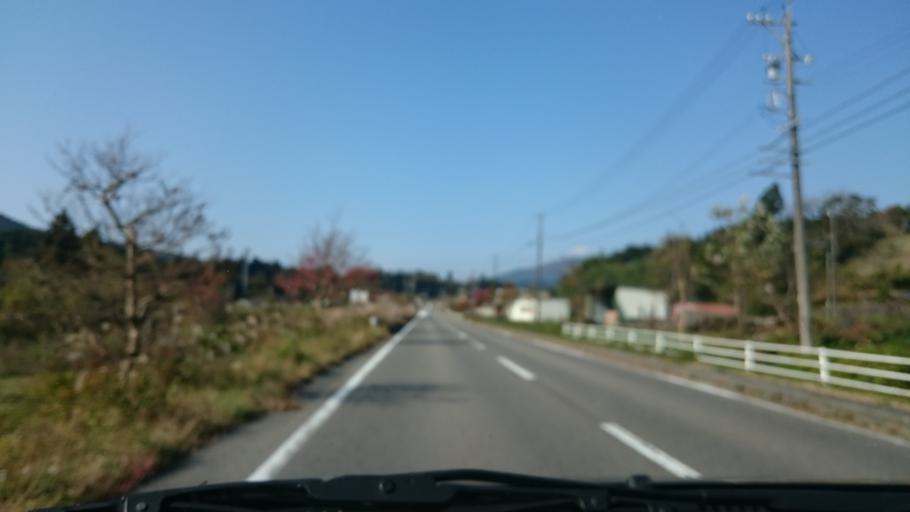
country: JP
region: Gifu
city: Nakatsugawa
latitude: 35.7324
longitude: 137.3461
